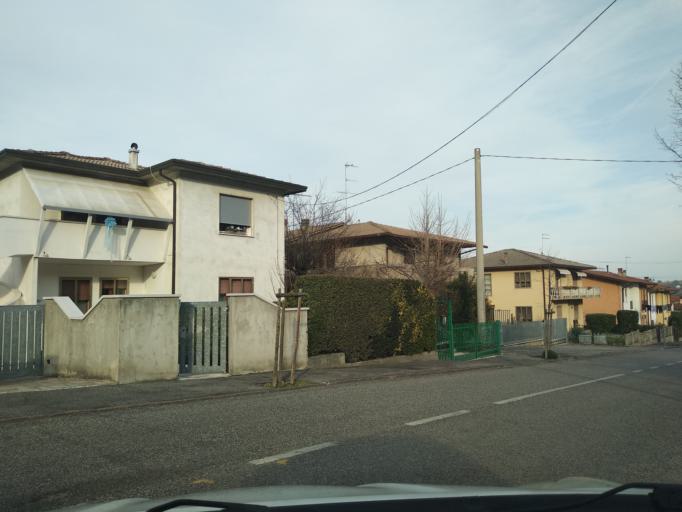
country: IT
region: Veneto
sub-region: Provincia di Vicenza
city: Barbarano Vicentino
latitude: 45.4084
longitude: 11.5400
